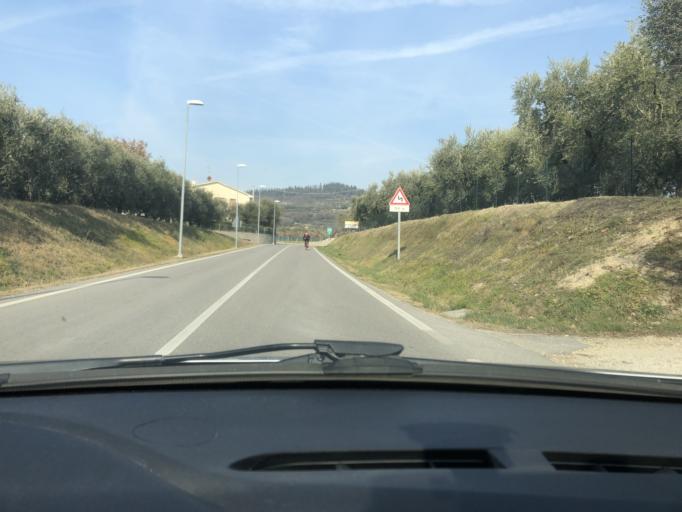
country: IT
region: Veneto
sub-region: Provincia di Verona
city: Bardolino
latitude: 45.5555
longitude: 10.7245
